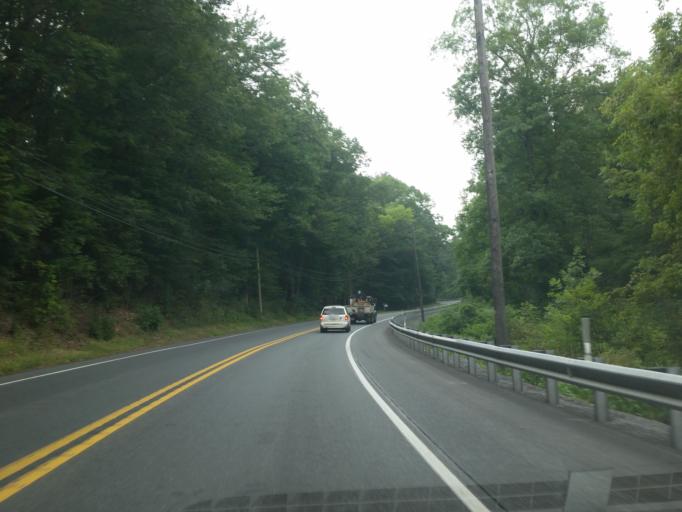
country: US
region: Pennsylvania
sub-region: Lancaster County
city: Brickerville
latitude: 40.2171
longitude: -76.3017
